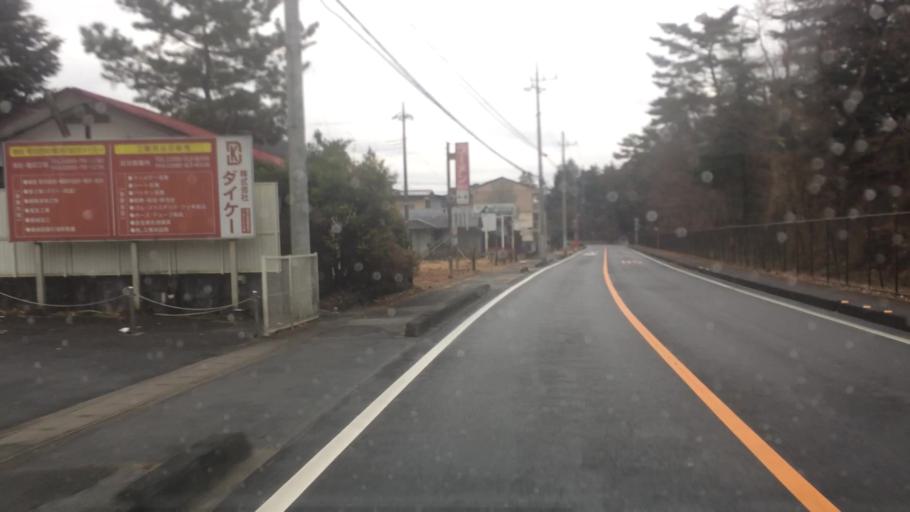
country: JP
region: Tochigi
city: Nikko
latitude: 36.7447
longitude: 139.6549
